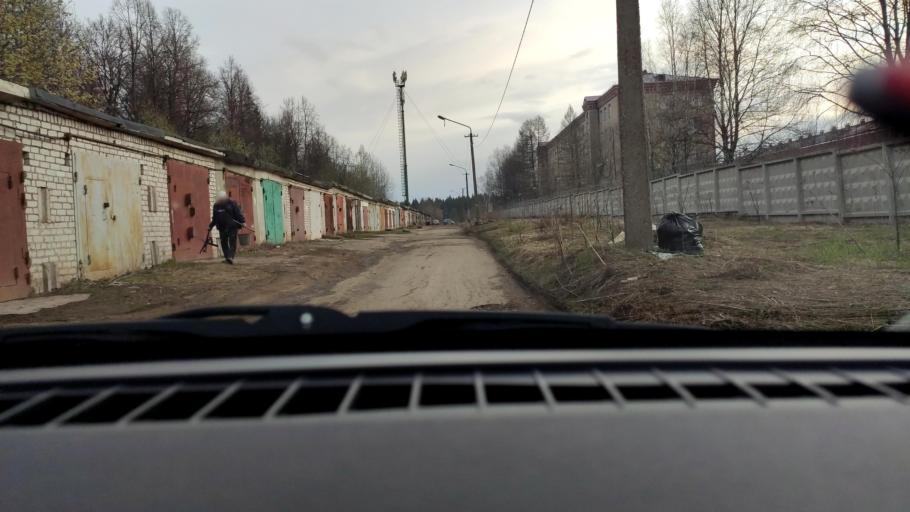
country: RU
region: Perm
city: Froly
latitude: 57.9718
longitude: 56.3209
